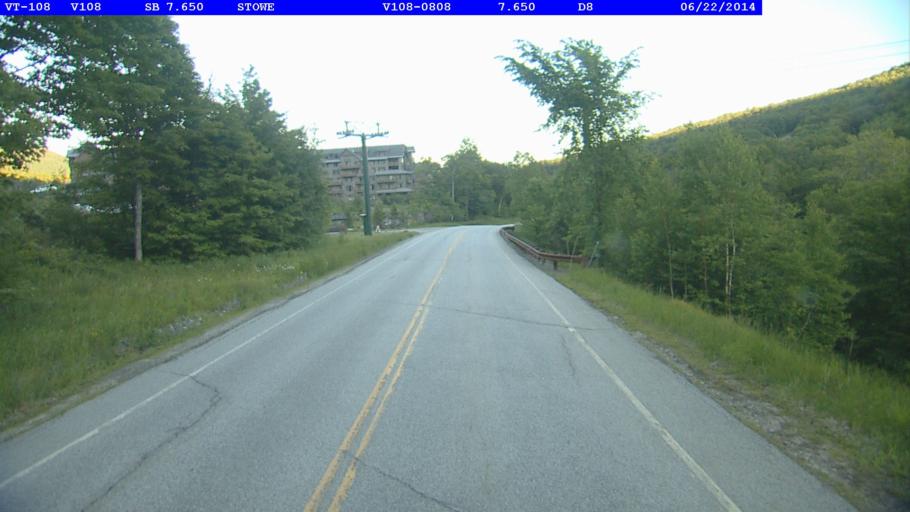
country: US
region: Vermont
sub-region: Lamoille County
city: Johnson
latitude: 44.5311
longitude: -72.7839
